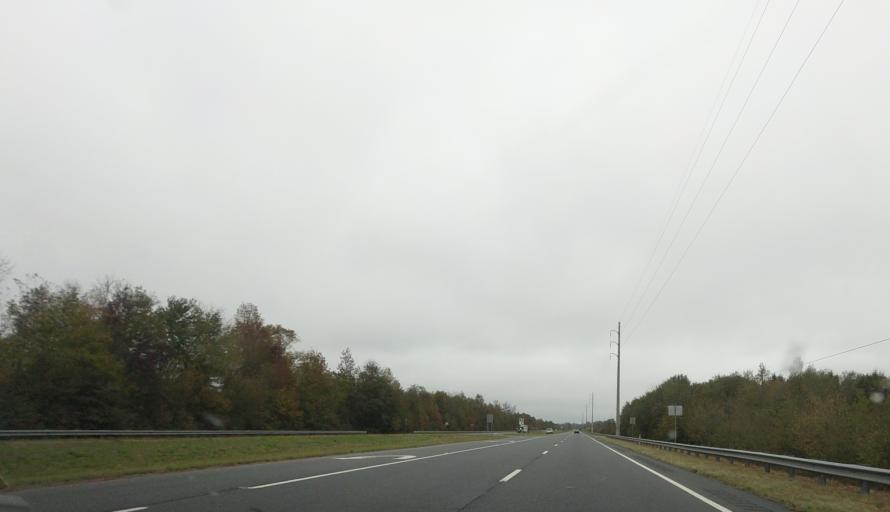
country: US
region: Georgia
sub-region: Taylor County
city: Reynolds
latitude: 32.5451
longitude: -84.0359
